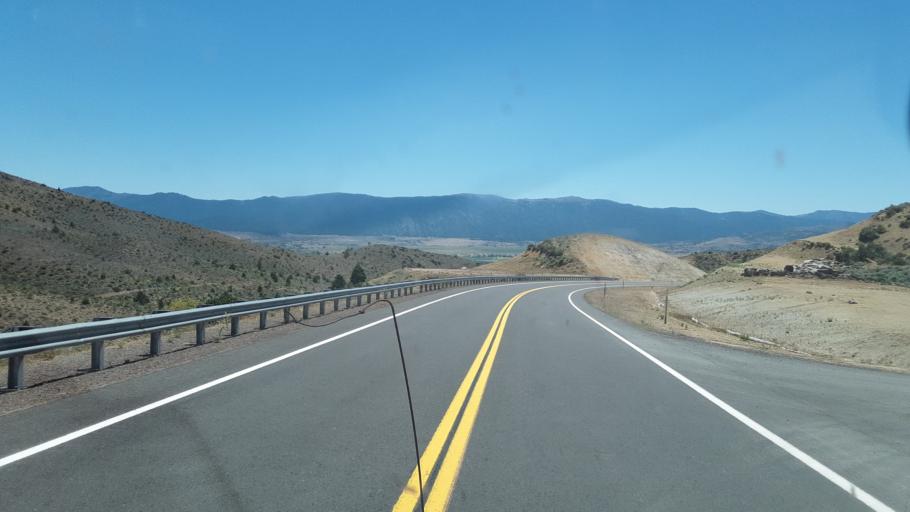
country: US
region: California
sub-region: Lassen County
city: Johnstonville
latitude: 40.4620
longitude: -120.5776
